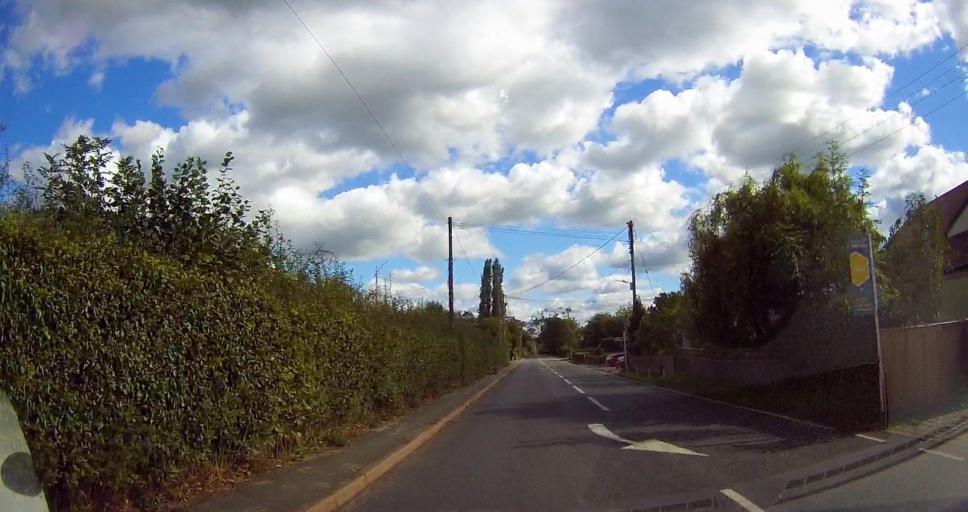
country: GB
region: England
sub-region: Cheshire East
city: Willaston
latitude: 52.9870
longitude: -2.4690
